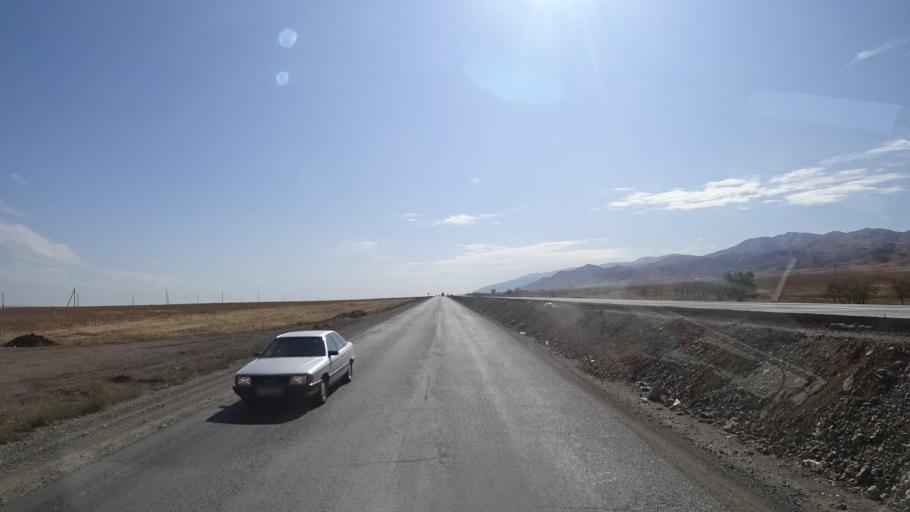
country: KG
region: Chuy
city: Ivanovka
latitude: 43.3991
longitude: 75.1182
